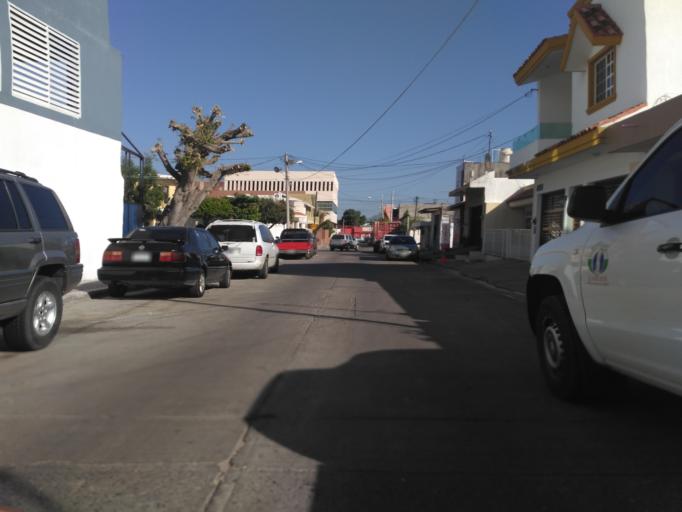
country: MX
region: Sinaloa
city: Culiacan
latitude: 24.7938
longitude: -107.4040
